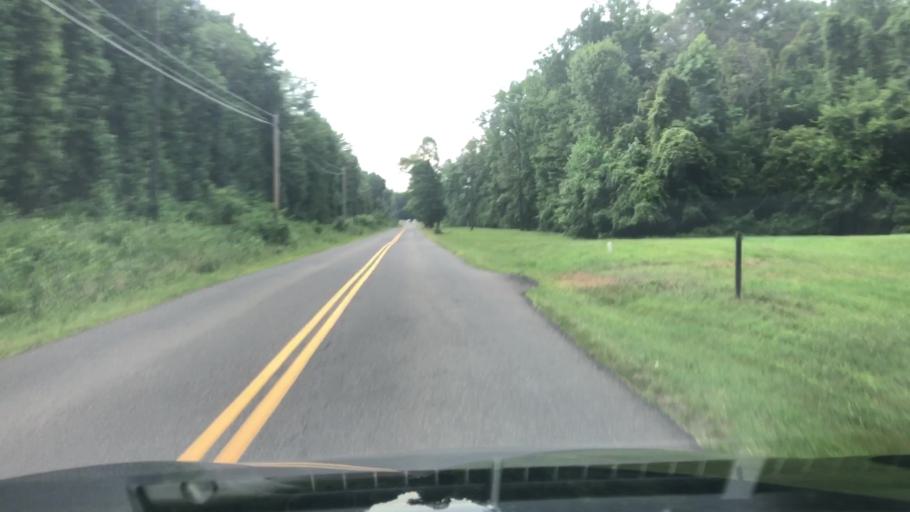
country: US
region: Virginia
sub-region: Fauquier County
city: New Baltimore
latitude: 38.7530
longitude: -77.6884
